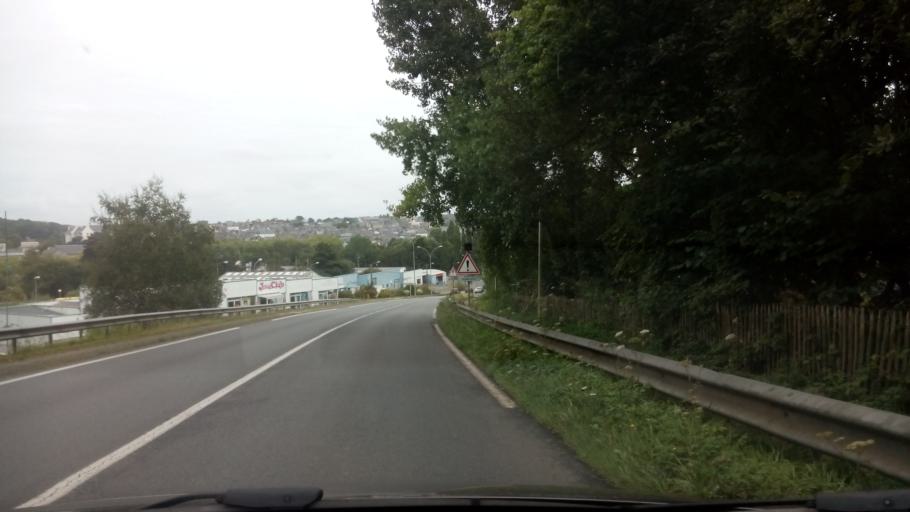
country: FR
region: Brittany
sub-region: Departement des Cotes-d'Armor
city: Lannion
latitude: 48.7305
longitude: -3.4705
